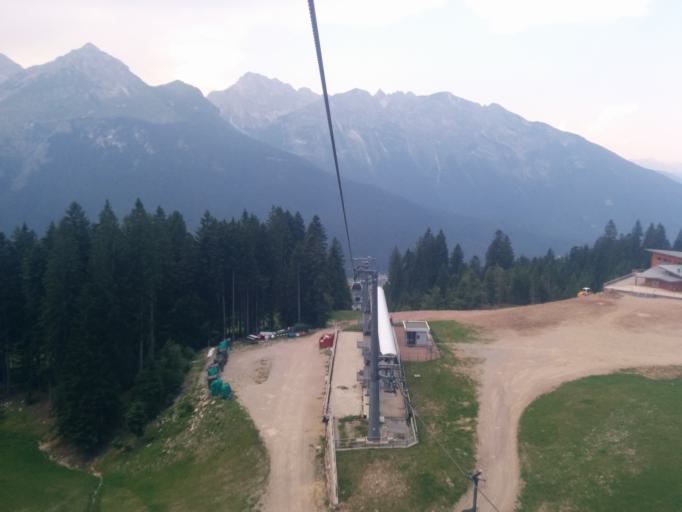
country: IT
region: Trentino-Alto Adige
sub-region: Provincia di Trento
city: Andalo
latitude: 46.1516
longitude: 11.0161
